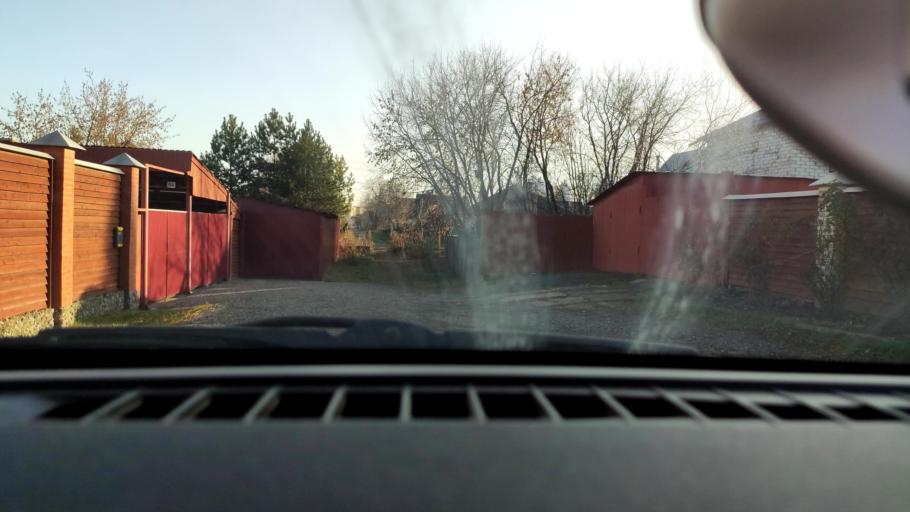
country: RU
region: Perm
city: Perm
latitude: 58.0167
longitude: 56.3191
